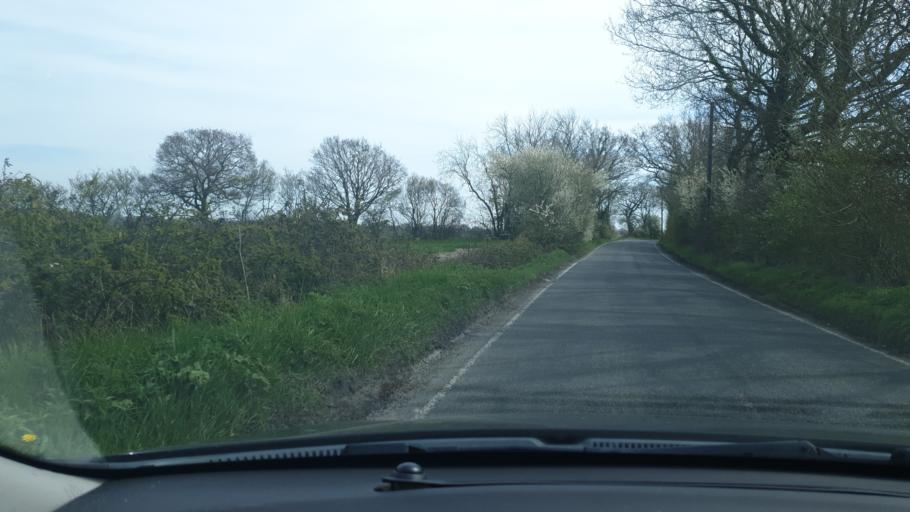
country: GB
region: England
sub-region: Essex
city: Little Clacton
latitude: 51.9076
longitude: 1.1721
